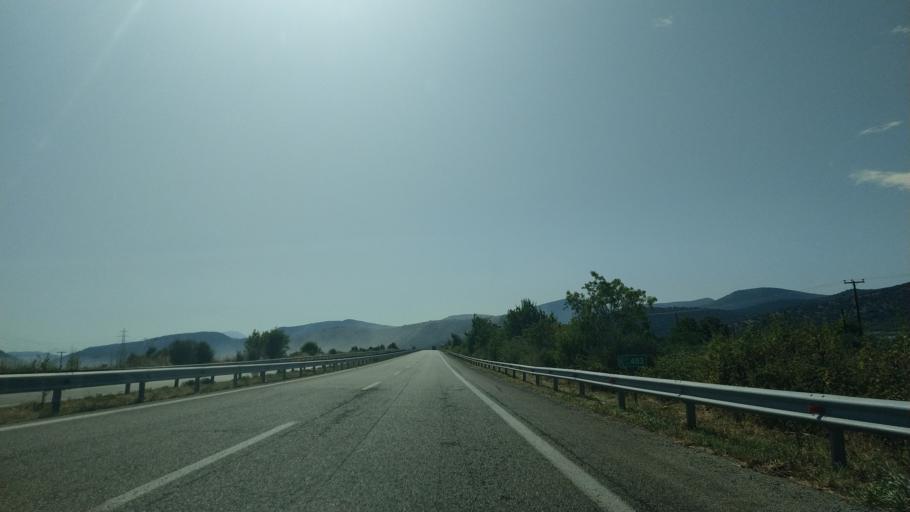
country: GR
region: East Macedonia and Thrace
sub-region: Nomos Kavalas
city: Nea Karvali
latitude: 40.9693
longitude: 24.5121
